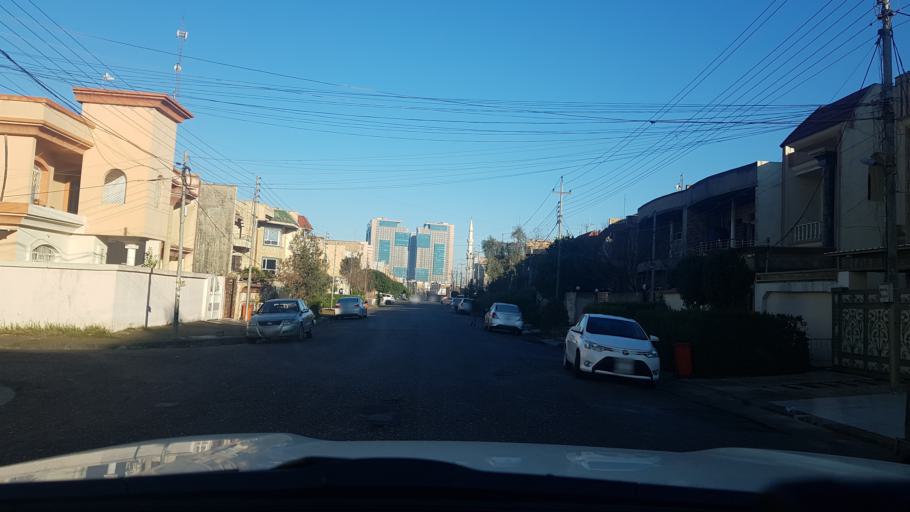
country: IQ
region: Arbil
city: Erbil
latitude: 36.2069
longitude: 44.0072
